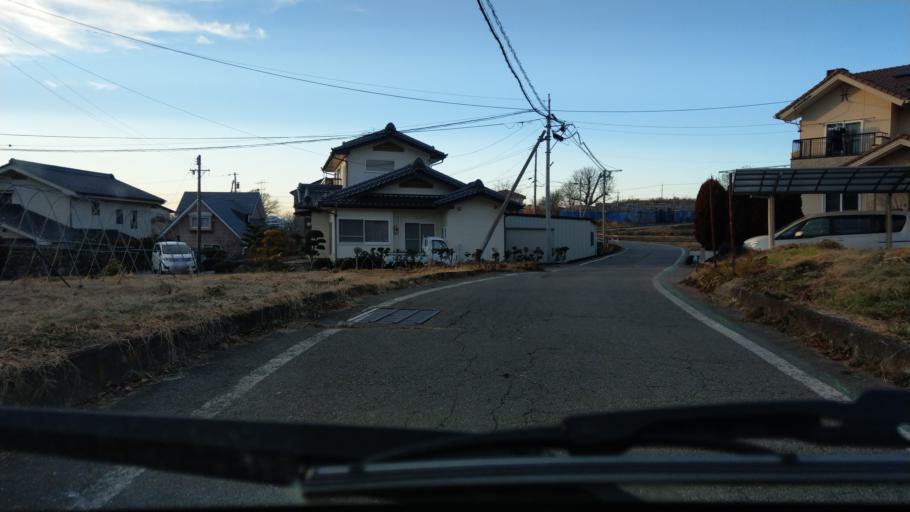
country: JP
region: Nagano
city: Komoro
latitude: 36.3427
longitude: 138.3911
